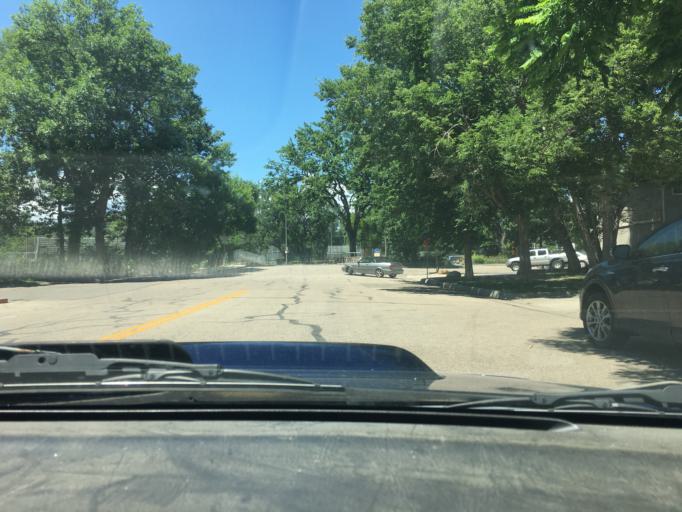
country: US
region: Colorado
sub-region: Larimer County
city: Fort Collins
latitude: 40.5857
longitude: -105.1053
